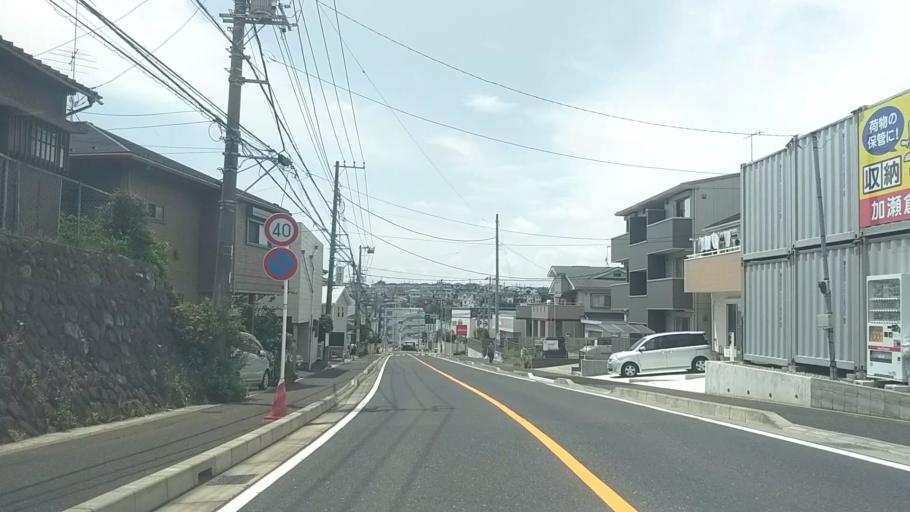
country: JP
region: Kanagawa
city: Fujisawa
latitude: 35.3493
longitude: 139.4987
